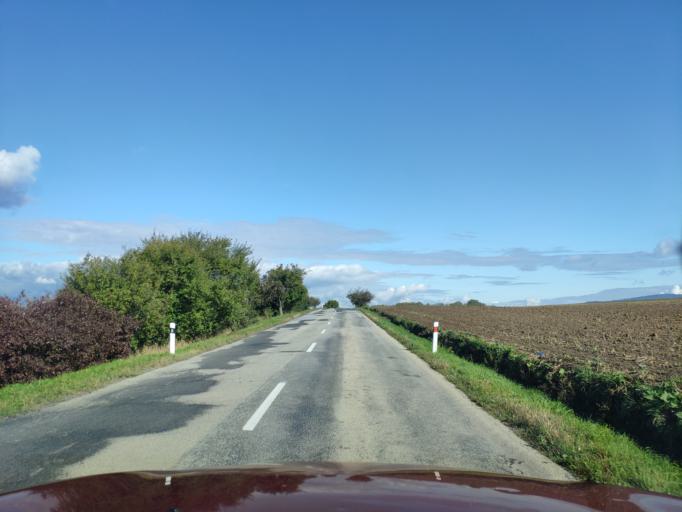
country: SK
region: Presovsky
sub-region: Okres Presov
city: Presov
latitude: 48.8963
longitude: 21.2593
